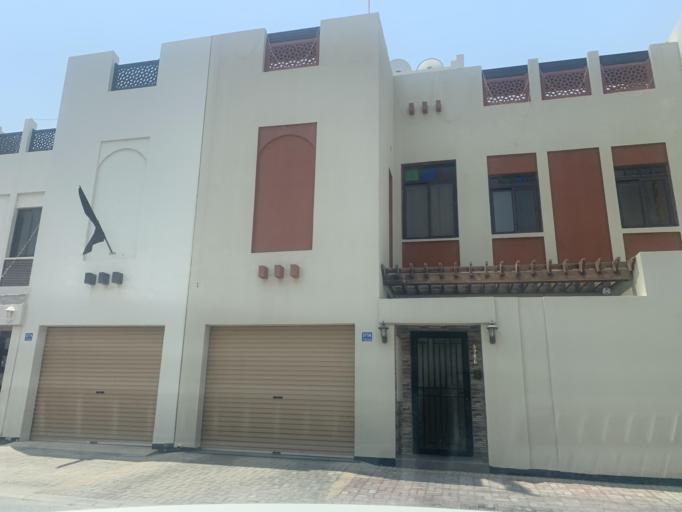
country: BH
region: Central Governorate
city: Madinat Hamad
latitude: 26.1465
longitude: 50.4627
